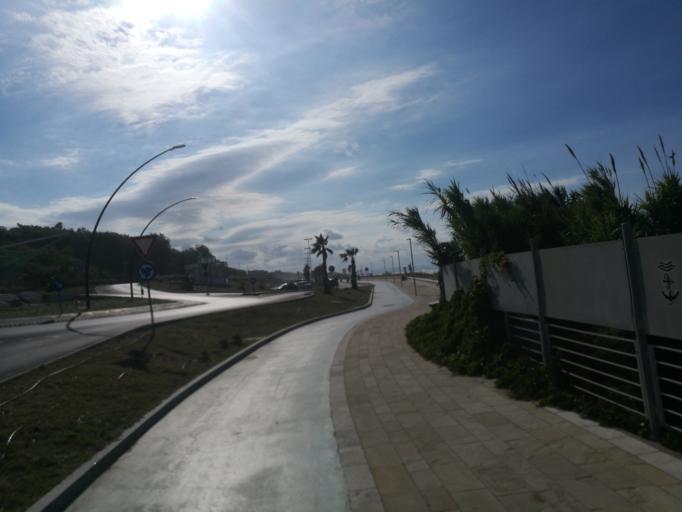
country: IT
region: Molise
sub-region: Provincia di Campobasso
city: Termoli
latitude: 42.0065
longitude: 14.9778
